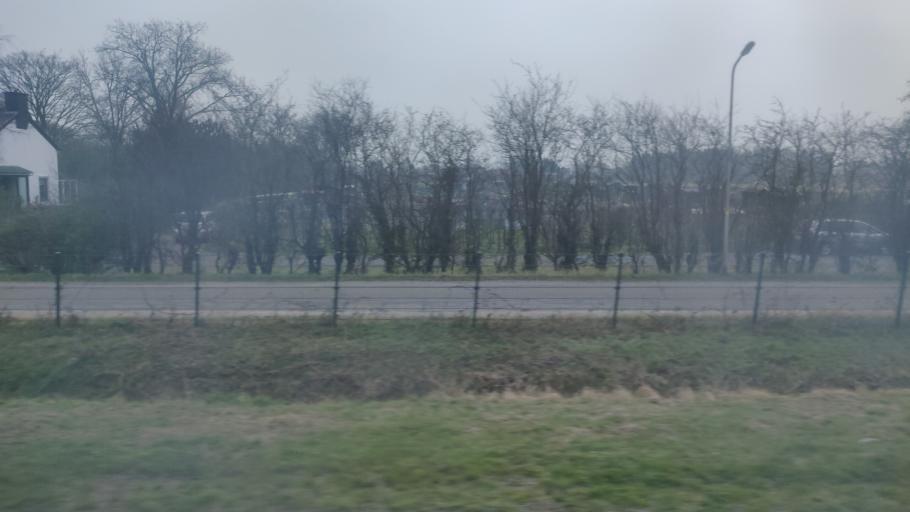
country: NL
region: North Holland
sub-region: Gemeente Heiloo
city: Heiloo
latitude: 52.5893
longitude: 4.6913
